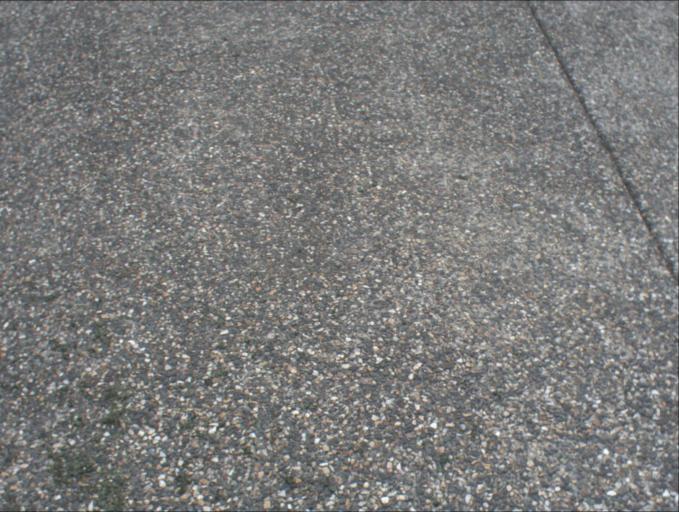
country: AU
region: Queensland
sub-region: Logan
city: Waterford West
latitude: -27.7133
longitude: 153.1446
